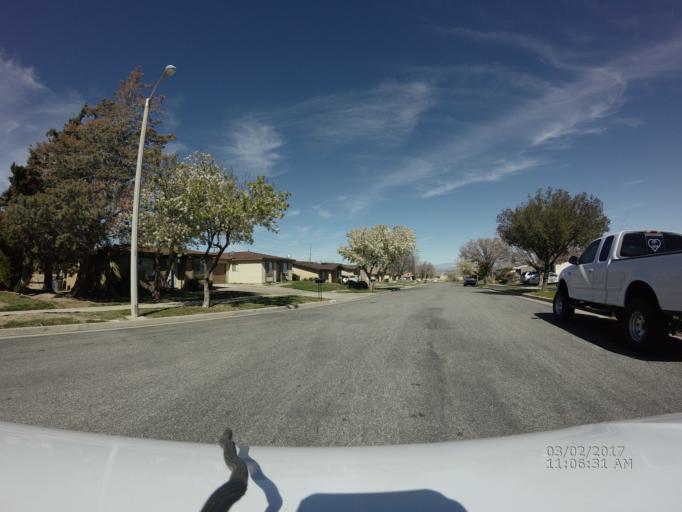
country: US
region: California
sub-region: Los Angeles County
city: Quartz Hill
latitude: 34.6464
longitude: -118.2529
